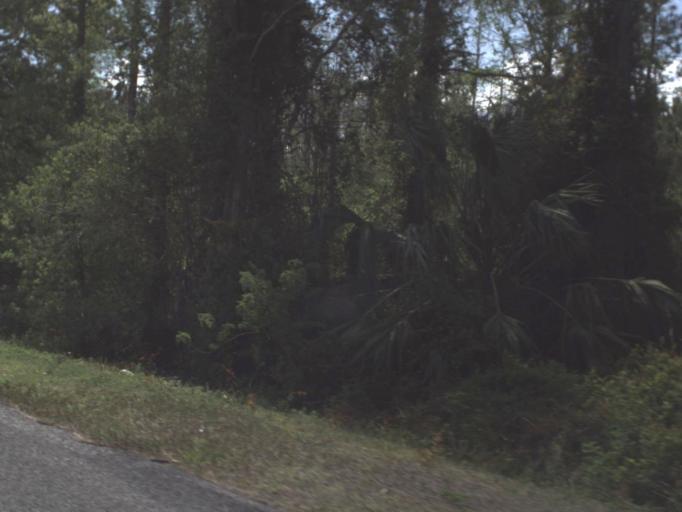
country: US
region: Florida
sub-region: Flagler County
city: Bunnell
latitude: 29.4094
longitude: -81.2016
